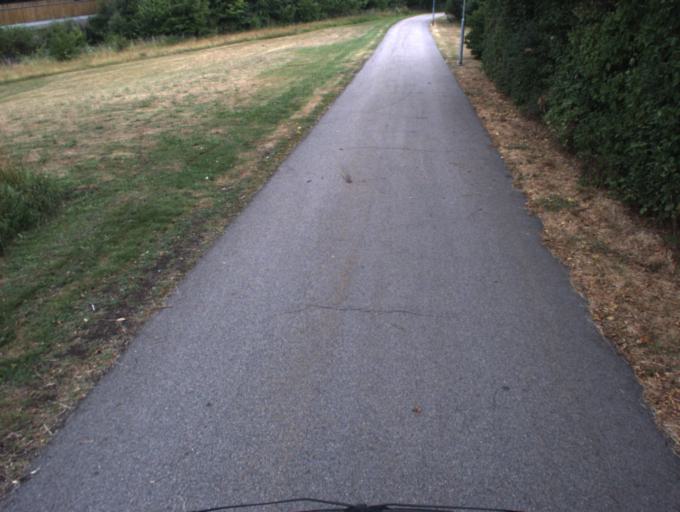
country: SE
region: Skane
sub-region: Helsingborg
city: Gantofta
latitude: 56.0215
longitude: 12.7601
